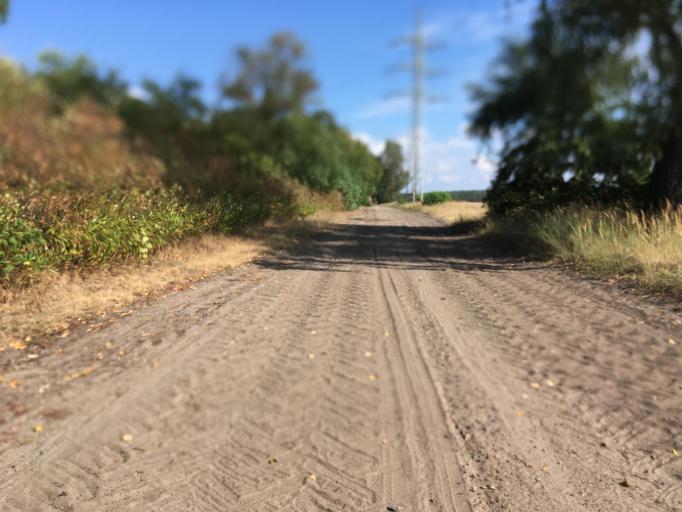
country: DE
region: Brandenburg
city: Zehdenick
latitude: 52.9573
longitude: 13.3821
